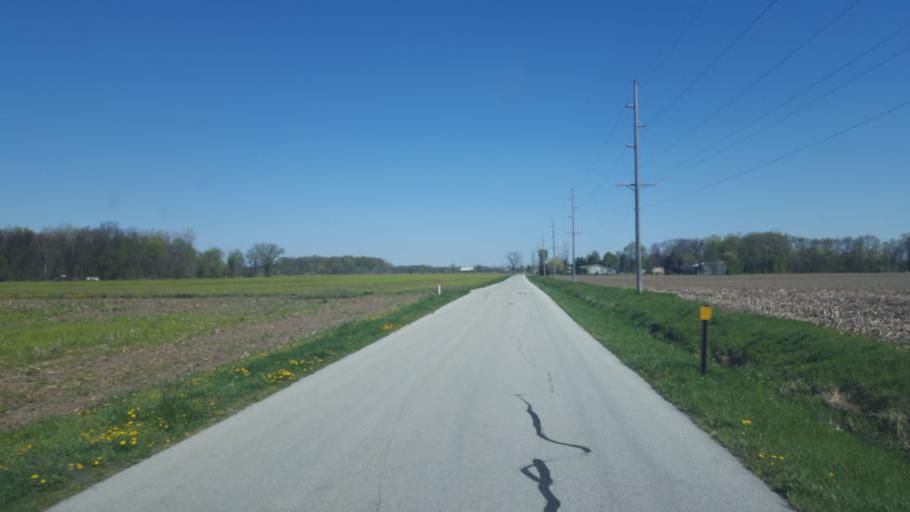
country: US
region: Ohio
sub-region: Sandusky County
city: Ballville
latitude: 41.2506
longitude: -83.1875
